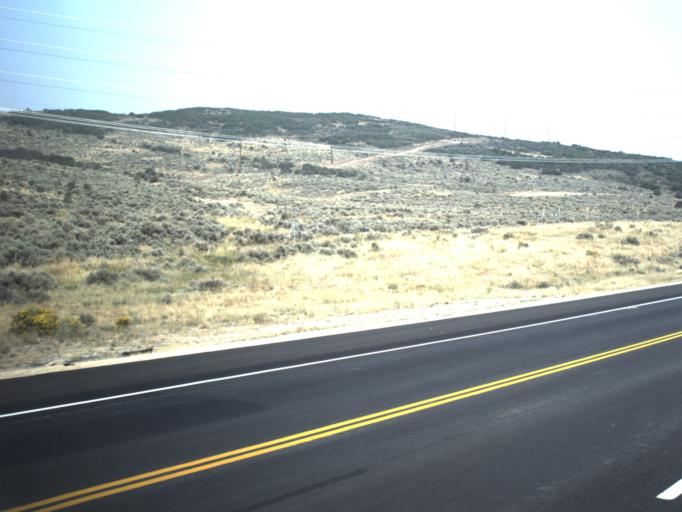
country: US
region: Utah
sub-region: Summit County
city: Park City
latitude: 40.6817
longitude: -111.4505
